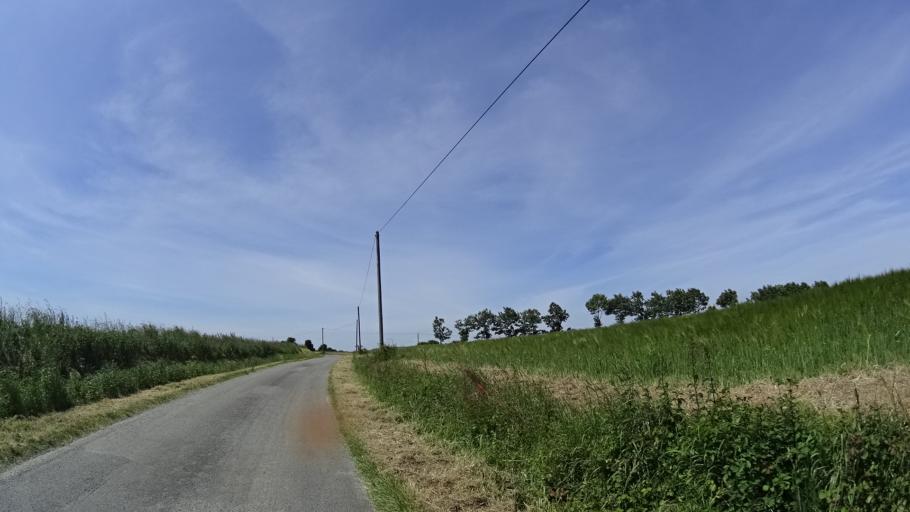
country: FR
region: Brittany
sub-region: Departement d'Ille-et-Vilaine
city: Iffendic
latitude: 48.1303
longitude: -2.0043
